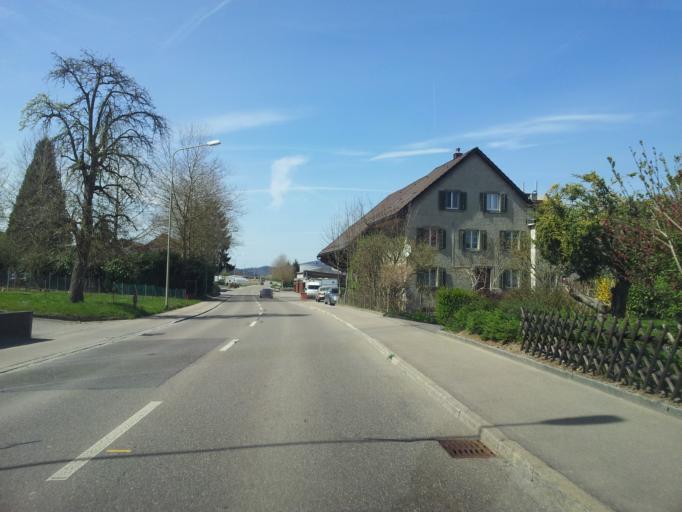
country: CH
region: Zurich
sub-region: Bezirk Dielsdorf
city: Daellikon / Daellikon (Dorf)
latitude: 47.4405
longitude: 8.4348
